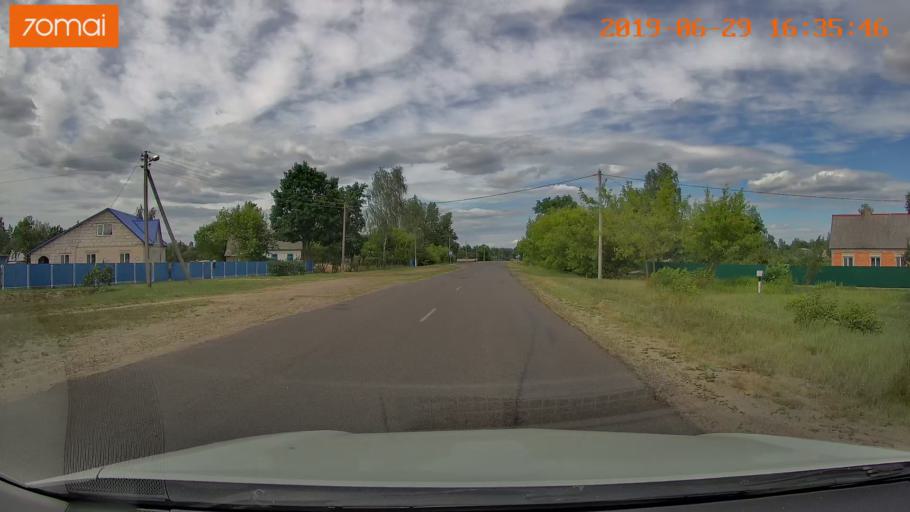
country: BY
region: Brest
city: Luninyets
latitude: 52.2153
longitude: 27.0185
